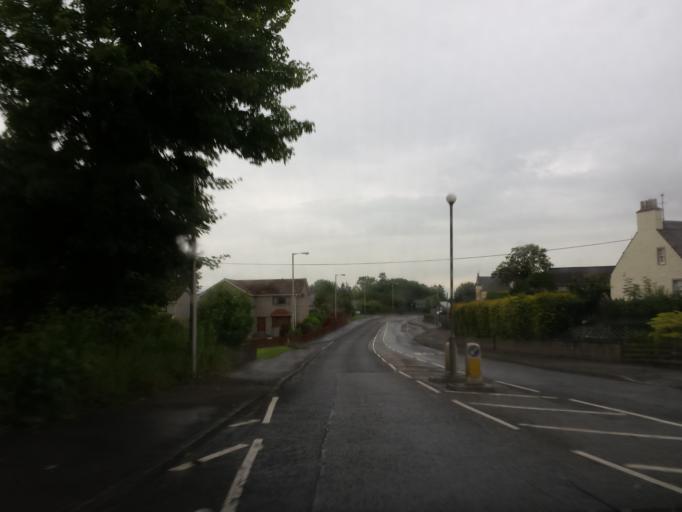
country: GB
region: Scotland
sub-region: Perth and Kinross
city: Abernethy
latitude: 56.3321
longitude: -3.3162
